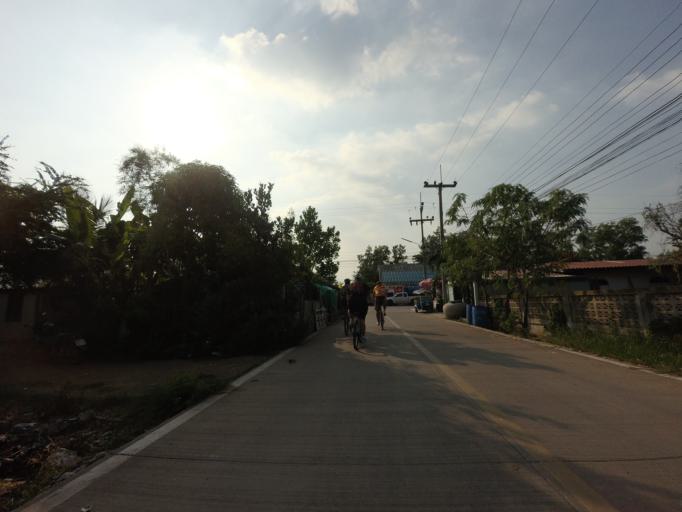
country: TH
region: Samut Sakhon
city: Samut Sakhon
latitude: 13.5079
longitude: 100.3072
